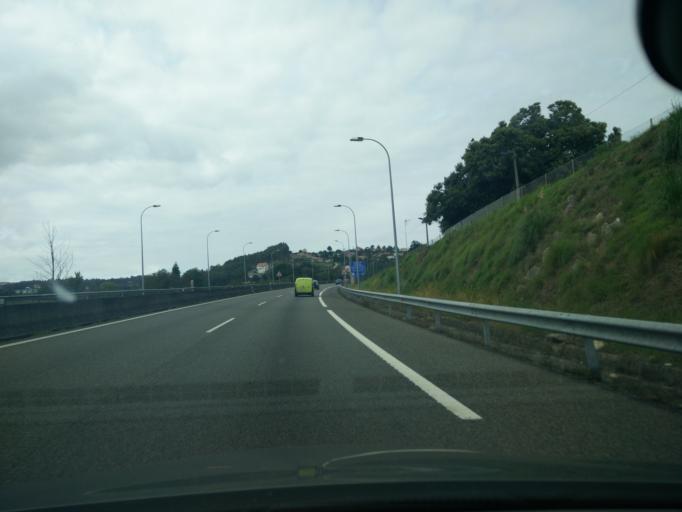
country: ES
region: Galicia
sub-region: Provincia da Coruna
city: Culleredo
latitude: 43.3145
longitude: -8.3876
